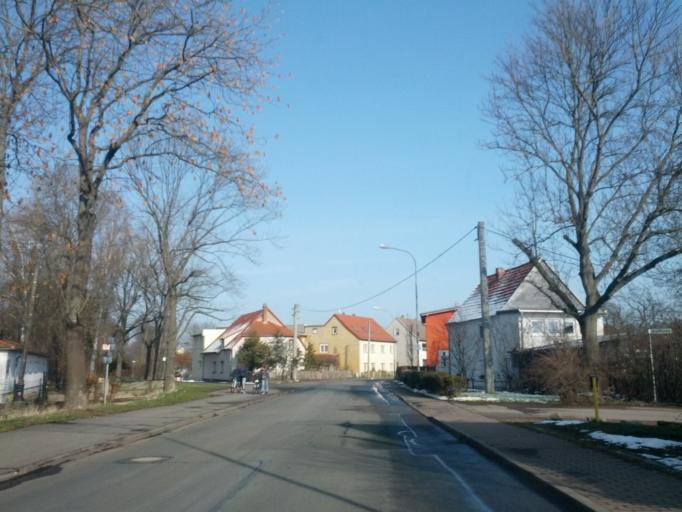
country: DE
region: Thuringia
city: Neudietendorf
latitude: 50.9072
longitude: 10.9090
